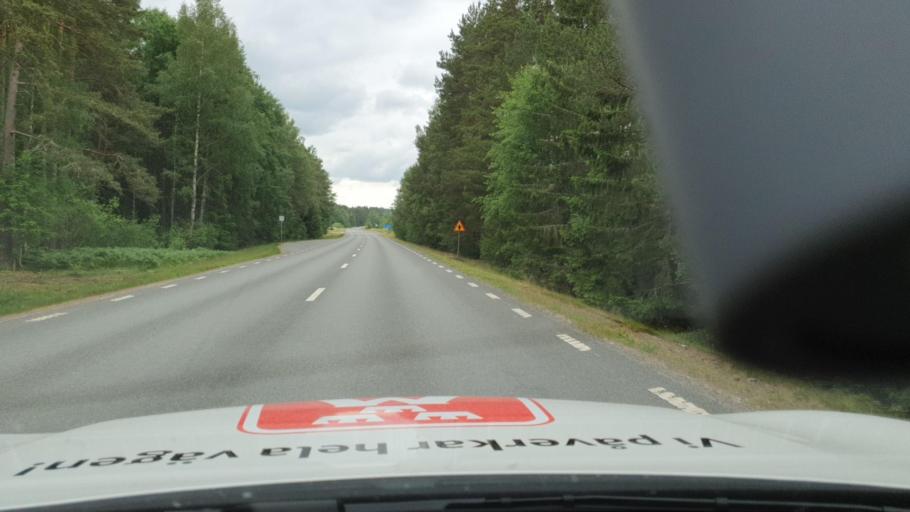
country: SE
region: Vaestra Goetaland
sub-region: Tidaholms Kommun
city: Olofstorp
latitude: 58.2229
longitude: 14.1121
